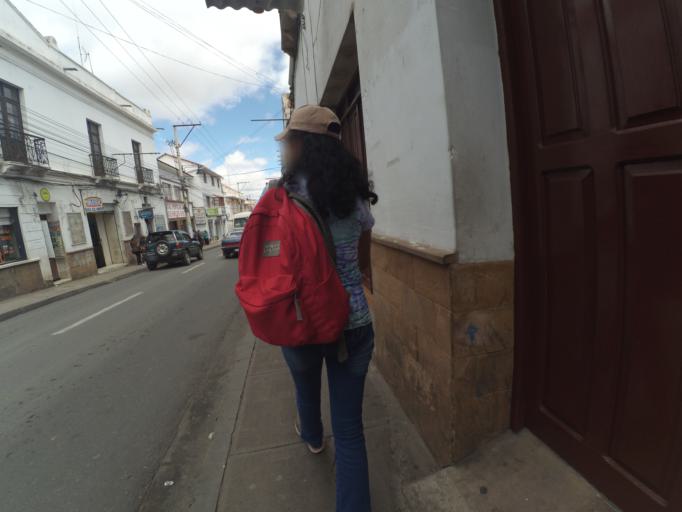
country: BO
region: Chuquisaca
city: Sucre
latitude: -19.0456
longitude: -65.2574
